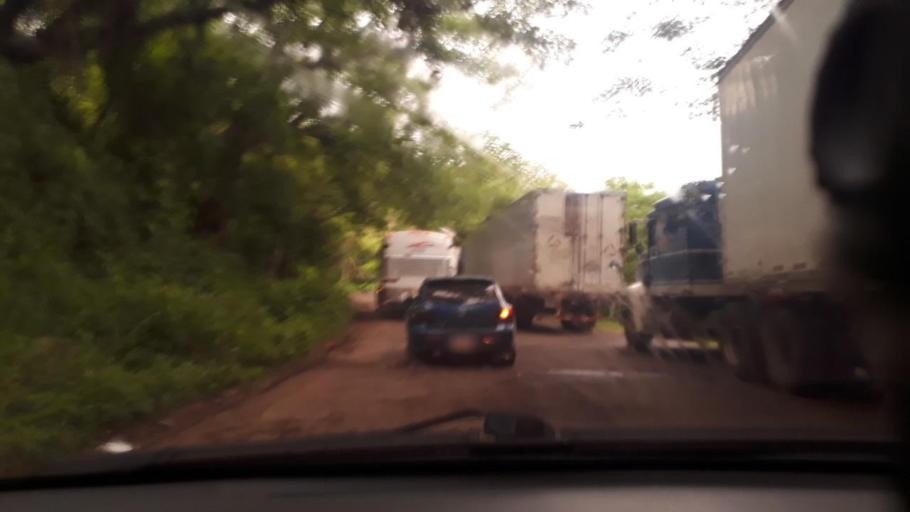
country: GT
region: Jutiapa
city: Atescatempa
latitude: 14.2168
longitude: -89.6914
